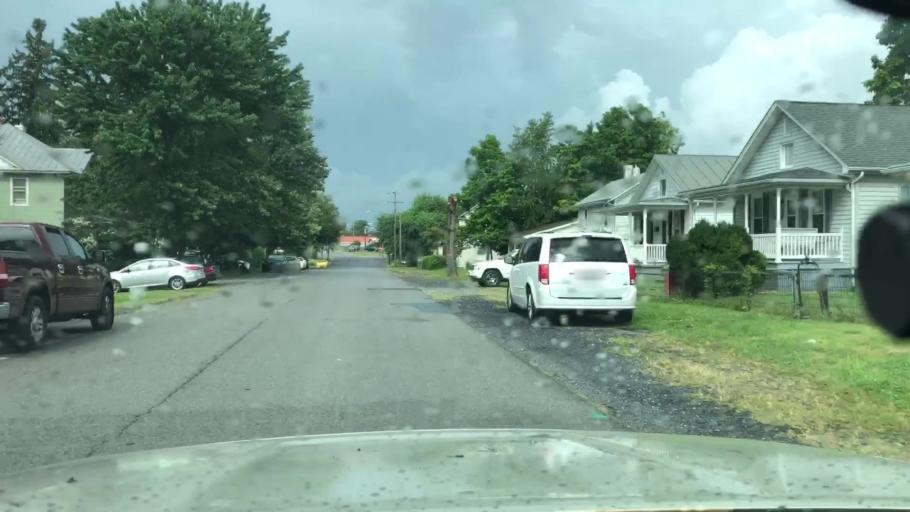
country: US
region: Virginia
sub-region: City of Waynesboro
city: Waynesboro
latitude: 38.0703
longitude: -78.9012
